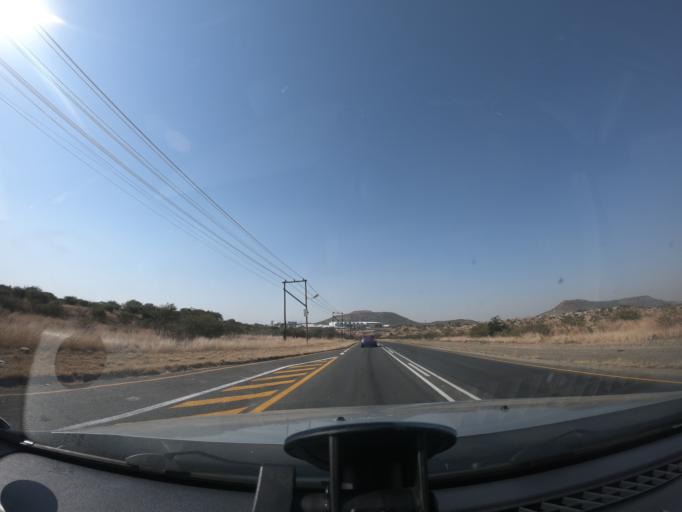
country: ZA
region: KwaZulu-Natal
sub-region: uThukela District Municipality
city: Ladysmith
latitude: -28.5470
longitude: 29.8228
